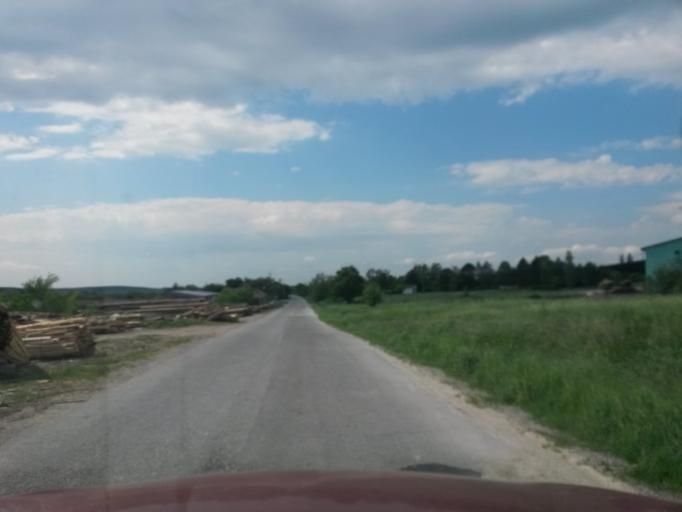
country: SK
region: Kosicky
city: Moldava nad Bodvou
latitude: 48.6988
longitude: 21.0129
